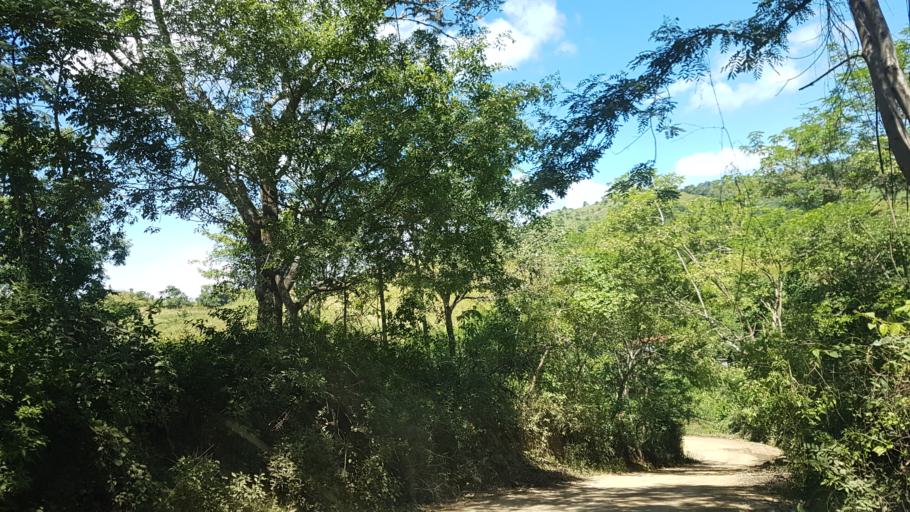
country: HN
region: El Paraiso
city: Santa Cruz
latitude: 13.7313
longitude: -86.6824
